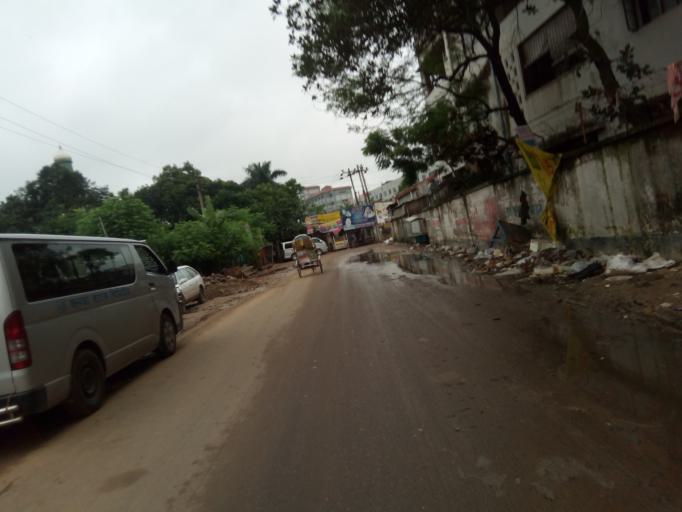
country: BD
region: Dhaka
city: Tungi
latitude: 23.8513
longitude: 90.4128
